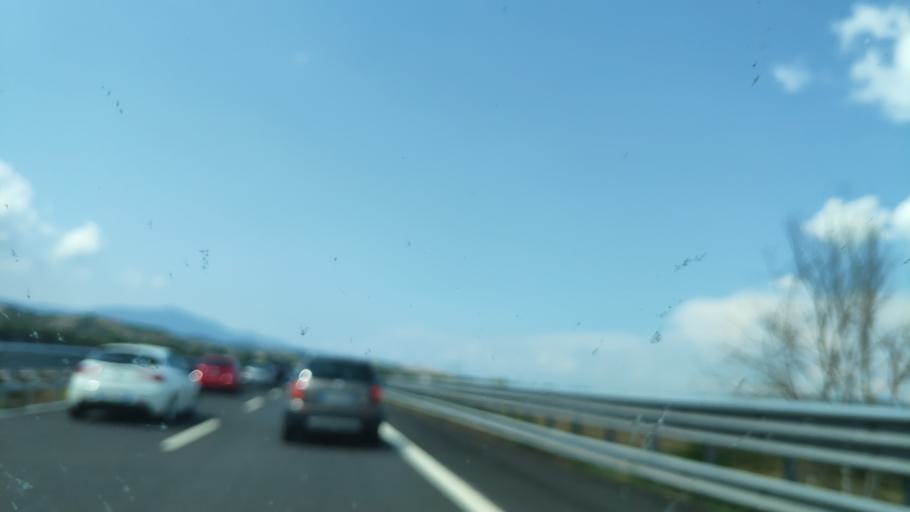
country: IT
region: Umbria
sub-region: Provincia di Terni
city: Fabro Scalo
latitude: 42.8622
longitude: 12.0362
